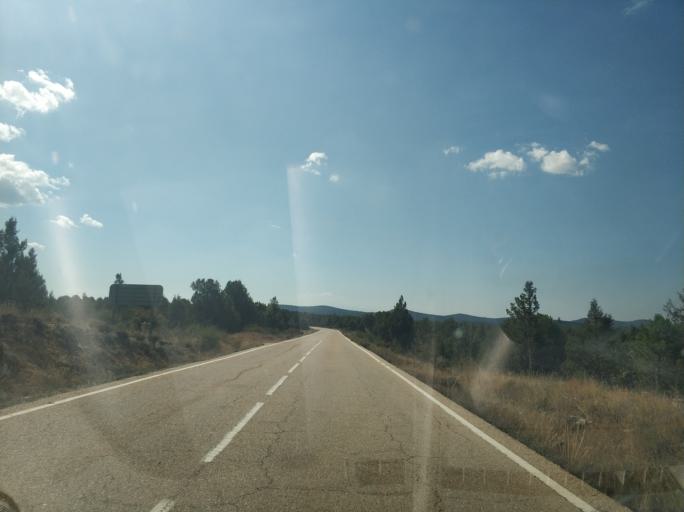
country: ES
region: Castille and Leon
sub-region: Provincia de Soria
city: Herrera de Soria
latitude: 41.7743
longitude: -3.0281
